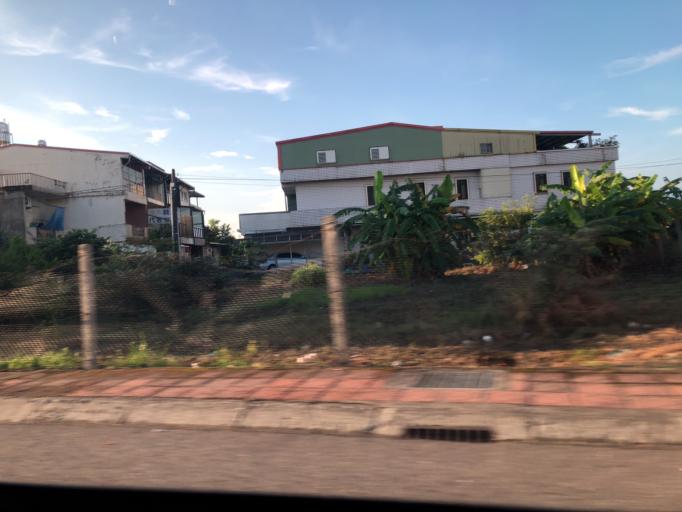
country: TW
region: Taiwan
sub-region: Yilan
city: Yilan
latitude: 24.7507
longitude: 121.7709
